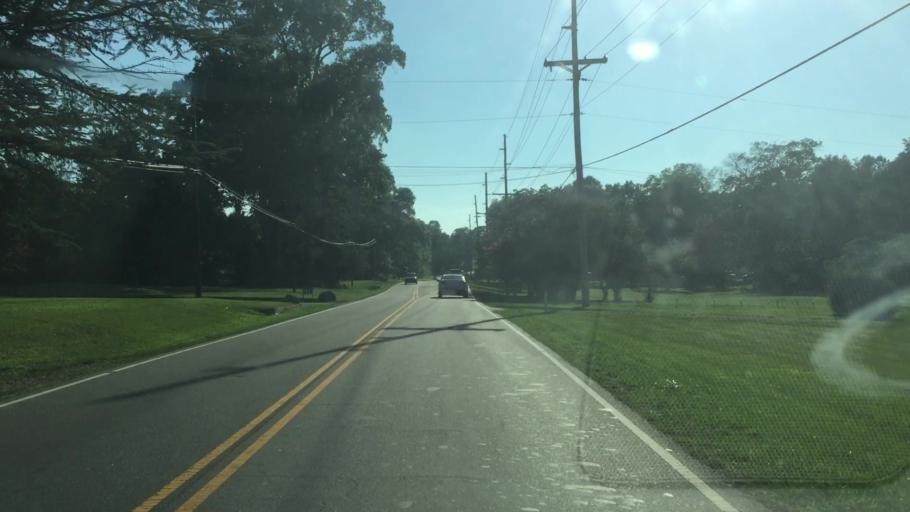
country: US
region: North Carolina
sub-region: Cabarrus County
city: Concord
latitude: 35.4126
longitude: -80.6185
